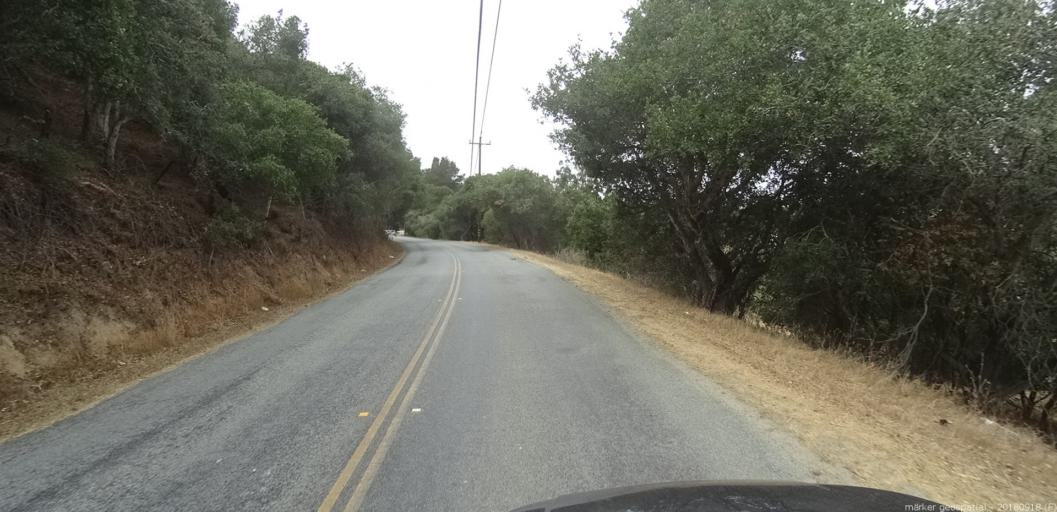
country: US
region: California
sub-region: Monterey County
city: Prunedale
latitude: 36.7784
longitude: -121.6500
